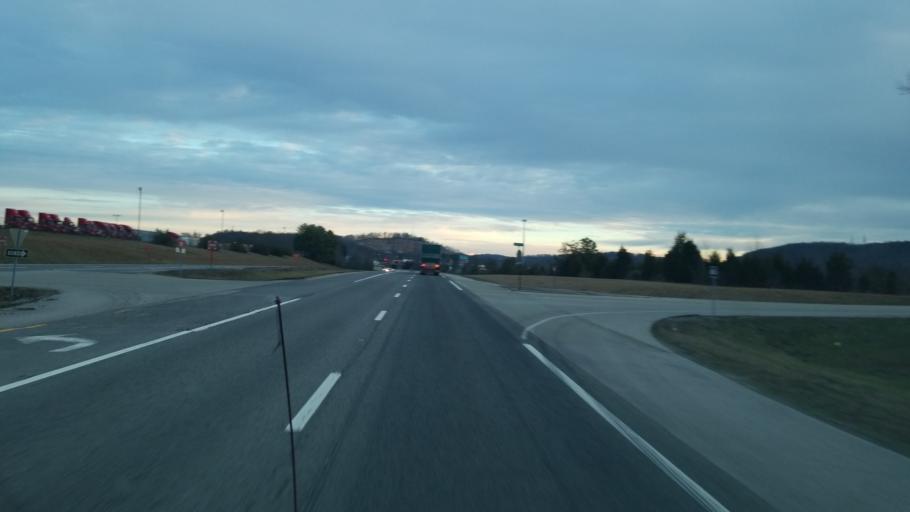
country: US
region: Tennessee
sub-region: Putnam County
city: Cookeville
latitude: 36.1236
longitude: -85.4862
